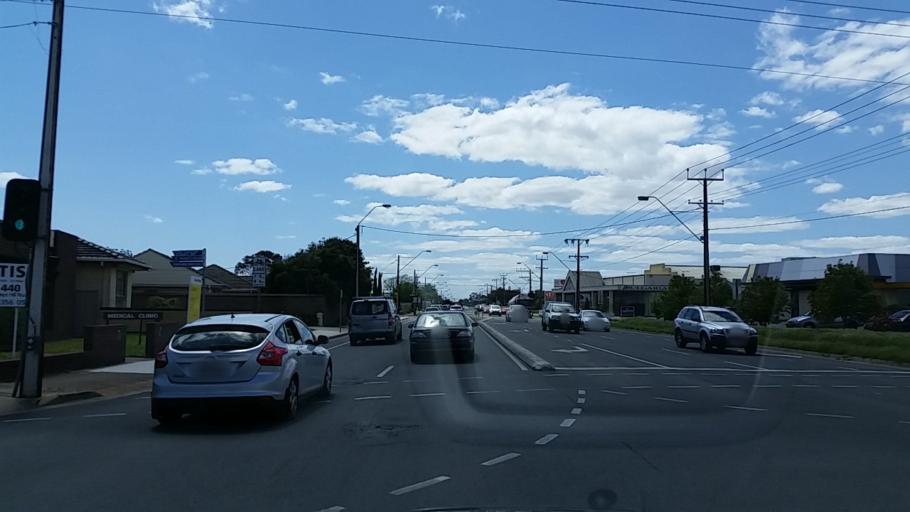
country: AU
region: South Australia
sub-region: Charles Sturt
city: Seaton
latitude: -34.9128
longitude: 138.5135
